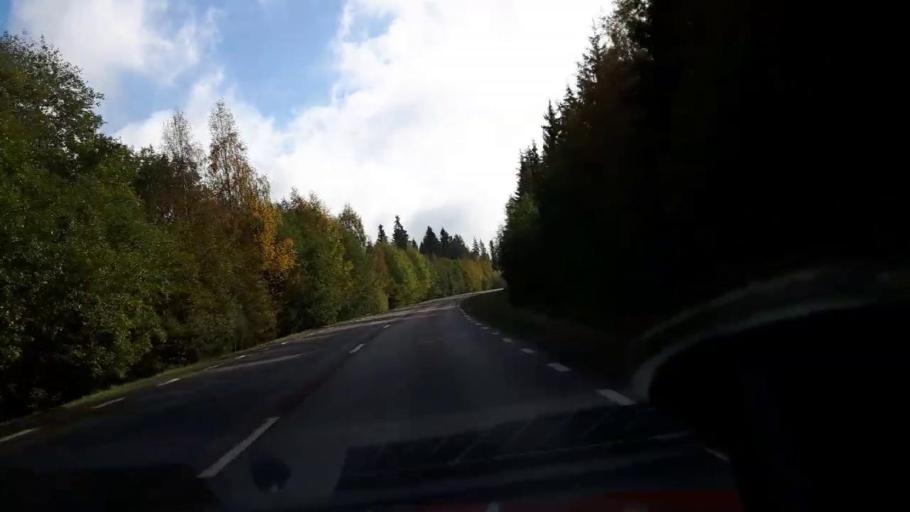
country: SE
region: Gaevleborg
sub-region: Ljusdals Kommun
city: Farila
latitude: 61.8863
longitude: 15.6995
